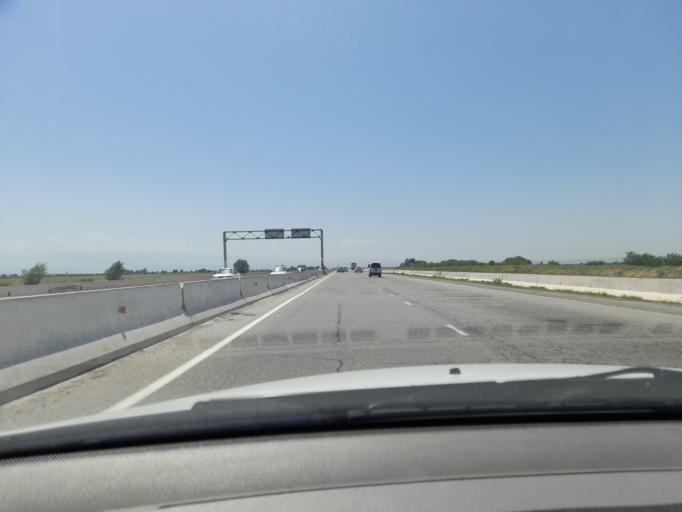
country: UZ
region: Jizzax
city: Paxtakor
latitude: 40.2402
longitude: 68.0063
